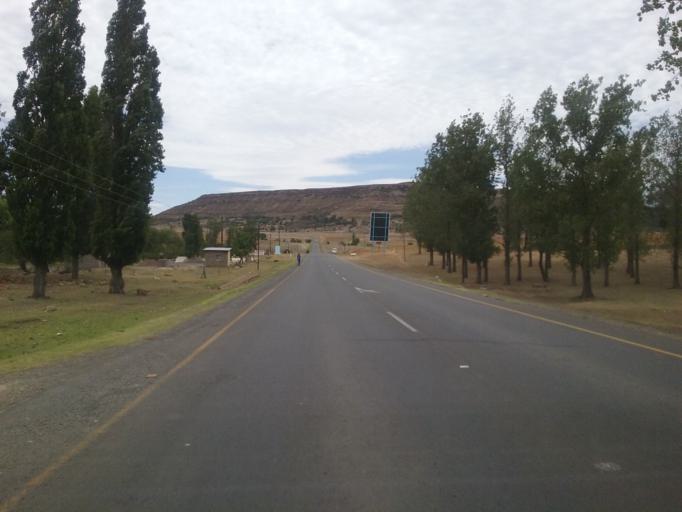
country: LS
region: Maseru
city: Nako
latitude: -29.6206
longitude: 27.4971
